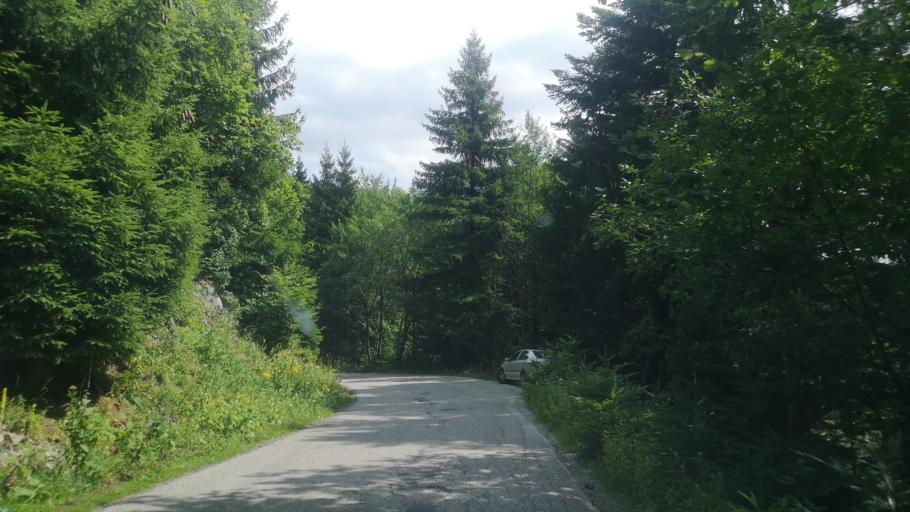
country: SK
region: Zilinsky
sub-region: Okres Zilina
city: Vrutky
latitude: 49.1053
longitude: 18.8574
